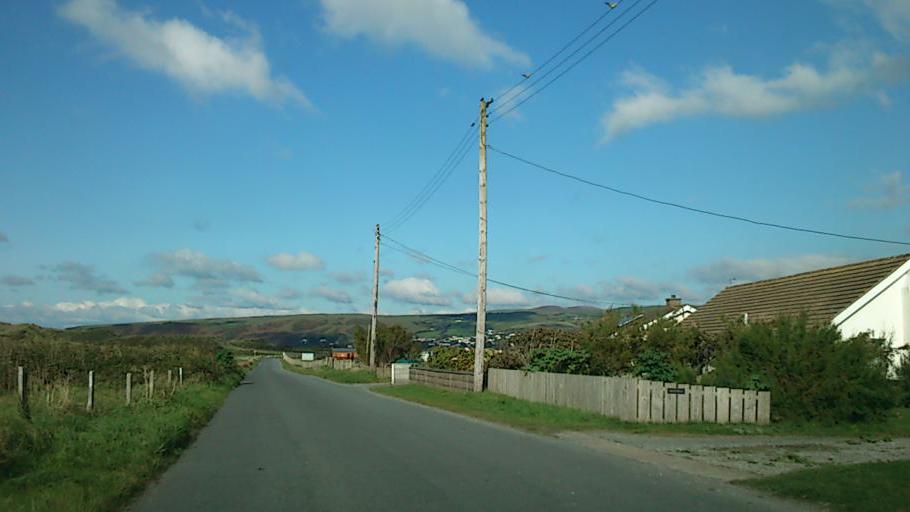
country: GB
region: Wales
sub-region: Gwynedd
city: Tywyn
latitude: 52.5183
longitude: -4.0536
